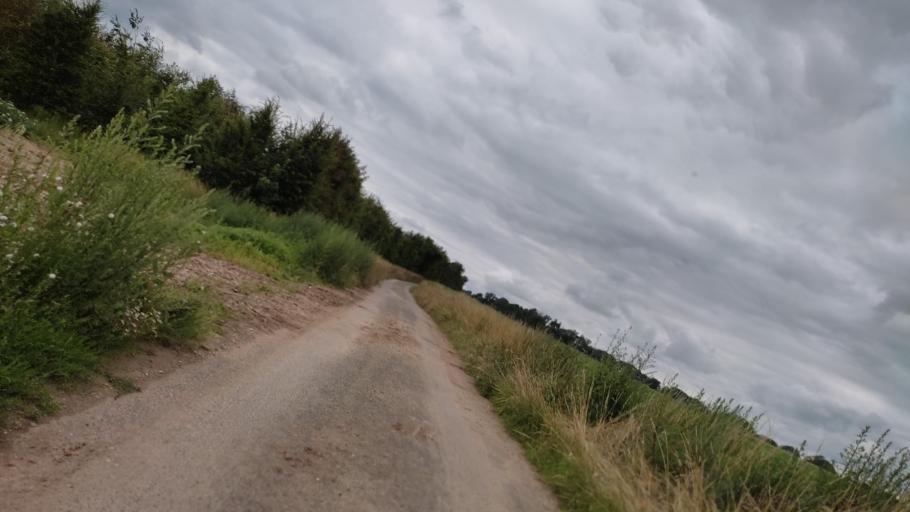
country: FR
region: Nord-Pas-de-Calais
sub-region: Departement du Pas-de-Calais
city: Beaumetz-les-Loges
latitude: 50.2605
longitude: 2.6583
